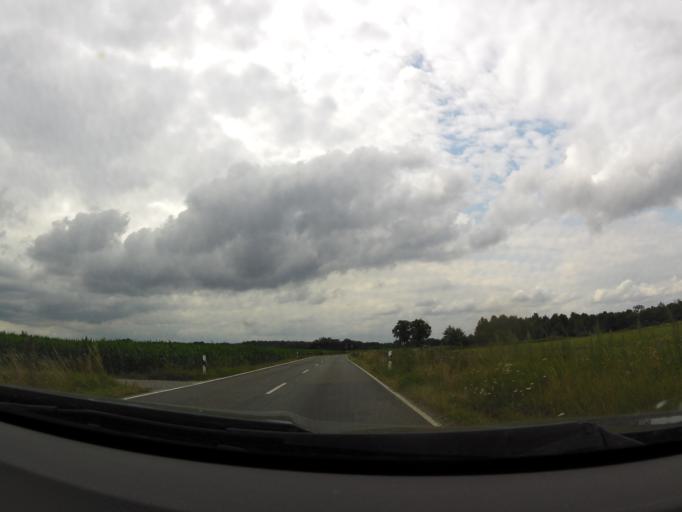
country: DE
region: North Rhine-Westphalia
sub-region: Regierungsbezirk Dusseldorf
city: Sonsbeck
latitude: 51.5916
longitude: 6.3215
